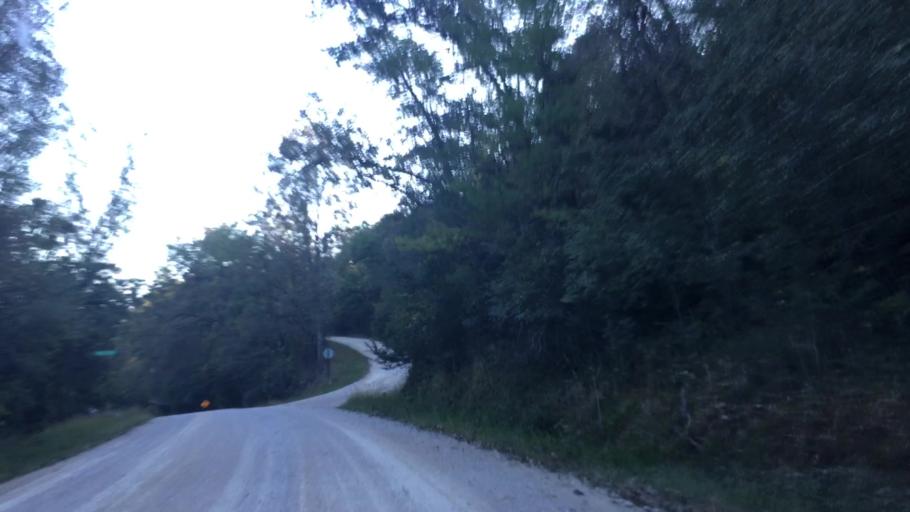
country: US
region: Minnesota
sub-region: Fillmore County
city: Preston
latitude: 43.7854
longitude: -92.0388
